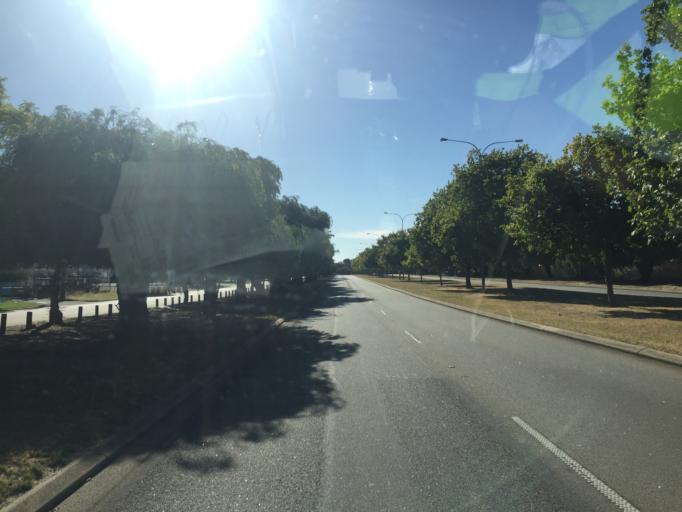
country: AU
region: Western Australia
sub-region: Canning
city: Queens Park
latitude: -31.9955
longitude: 115.9522
